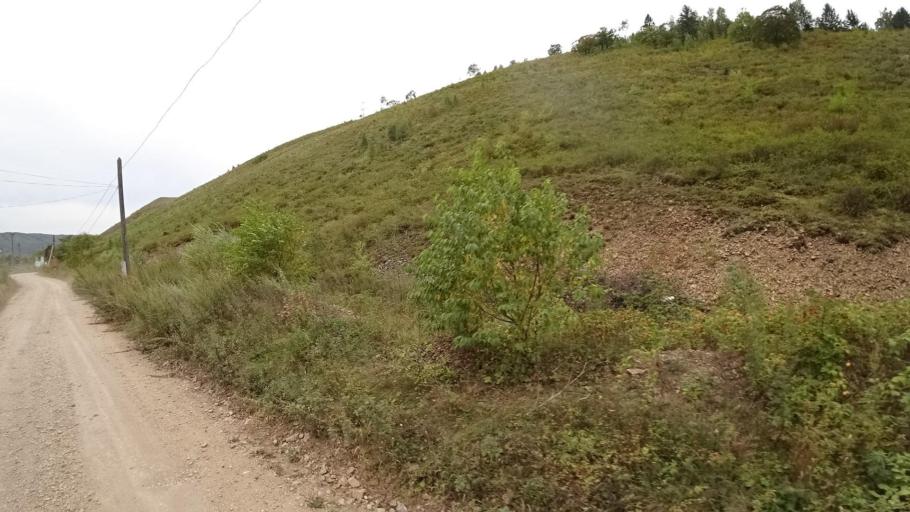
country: RU
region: Jewish Autonomous Oblast
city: Khingansk
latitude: 49.0268
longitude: 131.0748
